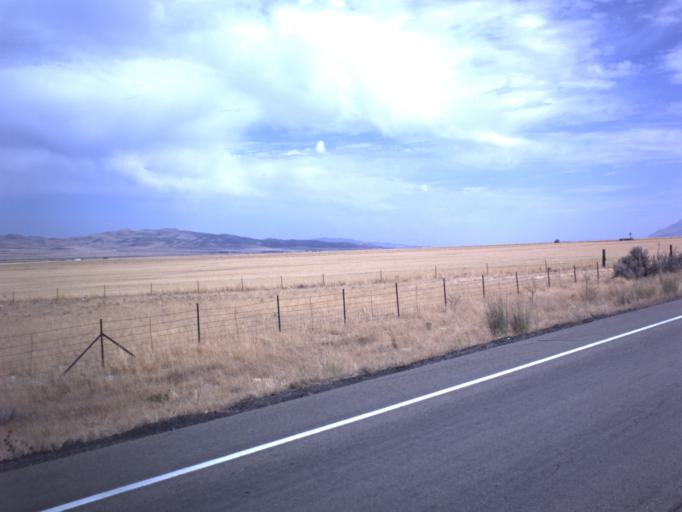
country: US
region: Utah
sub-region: Juab County
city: Nephi
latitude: 39.4917
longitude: -111.8819
